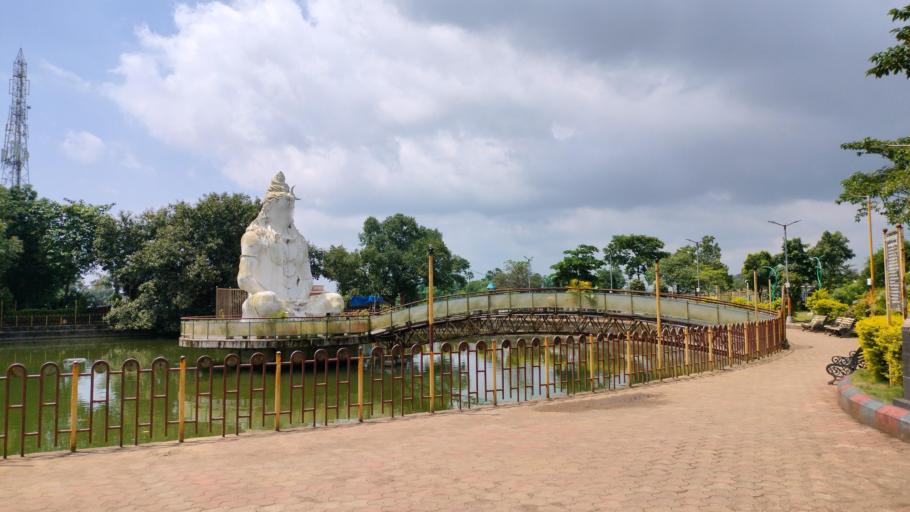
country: IN
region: Maharashtra
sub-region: Thane
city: Virar
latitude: 19.4665
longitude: 72.8473
